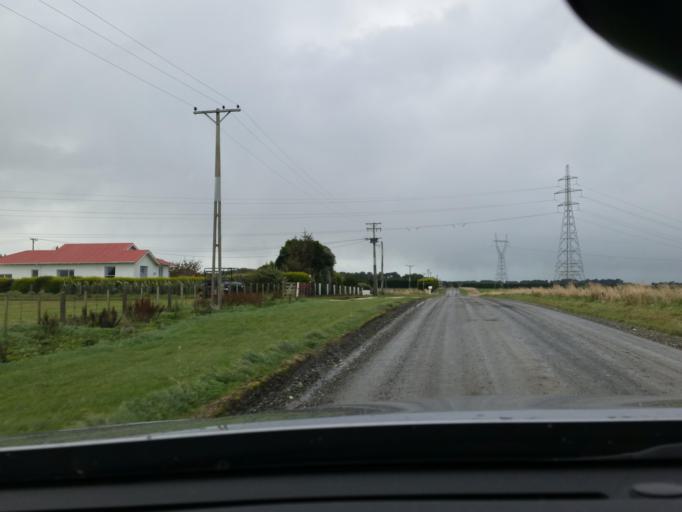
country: NZ
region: Southland
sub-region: Invercargill City
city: Invercargill
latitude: -46.3572
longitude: 168.4210
